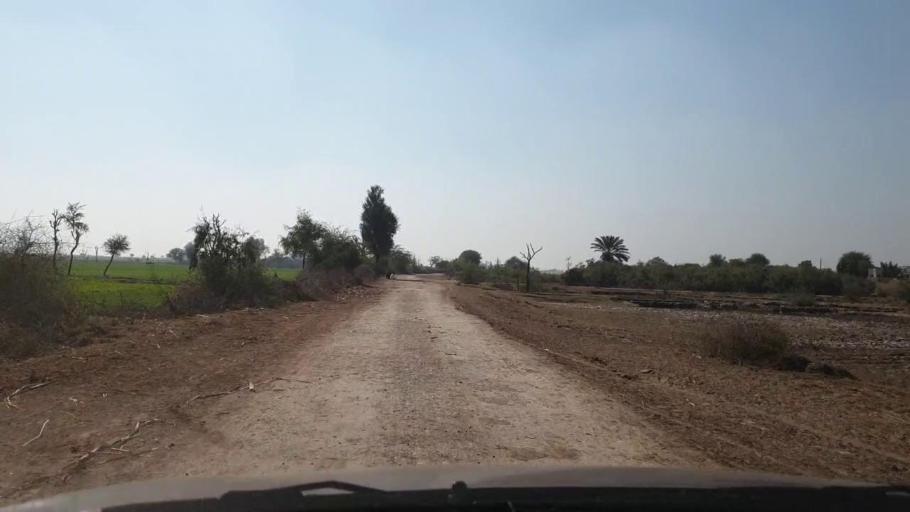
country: PK
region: Sindh
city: Jhol
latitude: 25.9230
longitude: 68.7946
